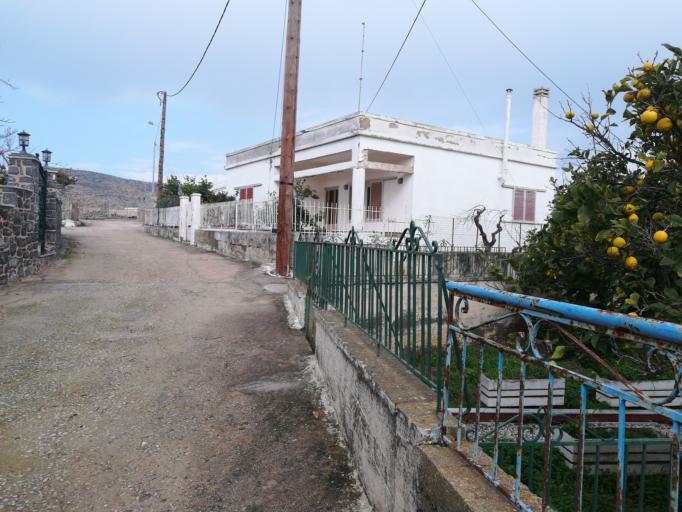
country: GR
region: North Aegean
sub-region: Chios
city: Thymiana
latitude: 38.2483
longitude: 25.9435
